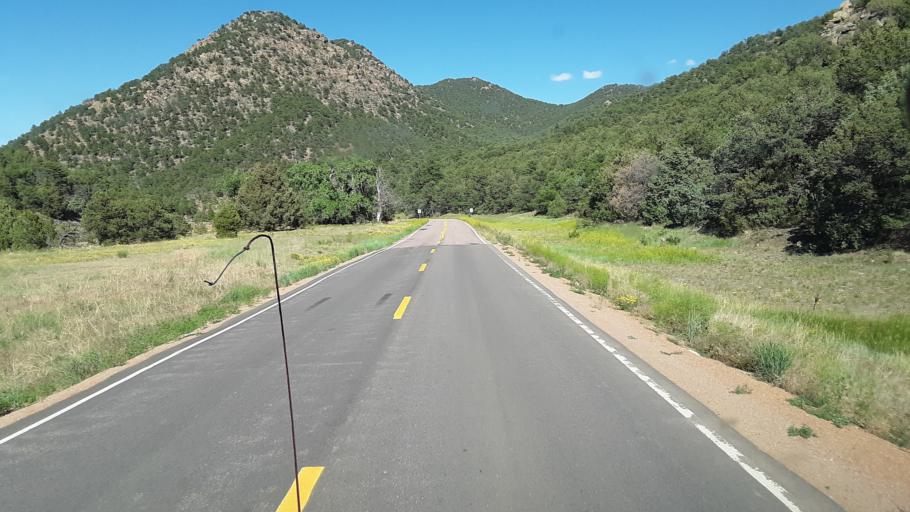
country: US
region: Colorado
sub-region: Fremont County
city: Canon City
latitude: 38.4123
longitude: -105.4183
